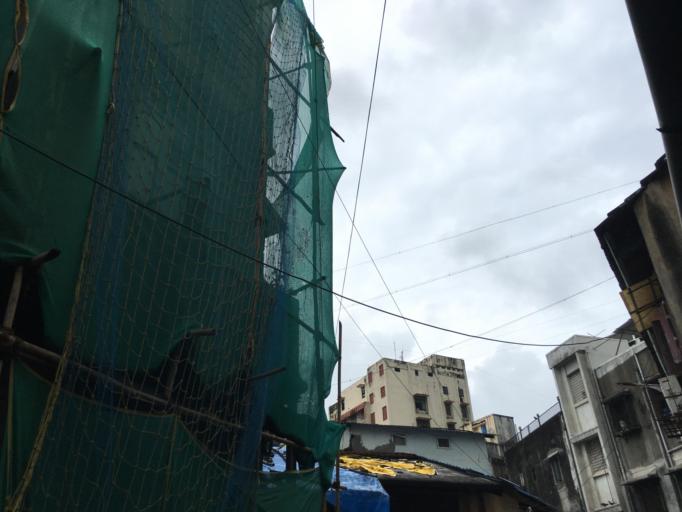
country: IN
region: Maharashtra
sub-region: Mumbai Suburban
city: Mumbai
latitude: 18.9514
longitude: 72.8243
